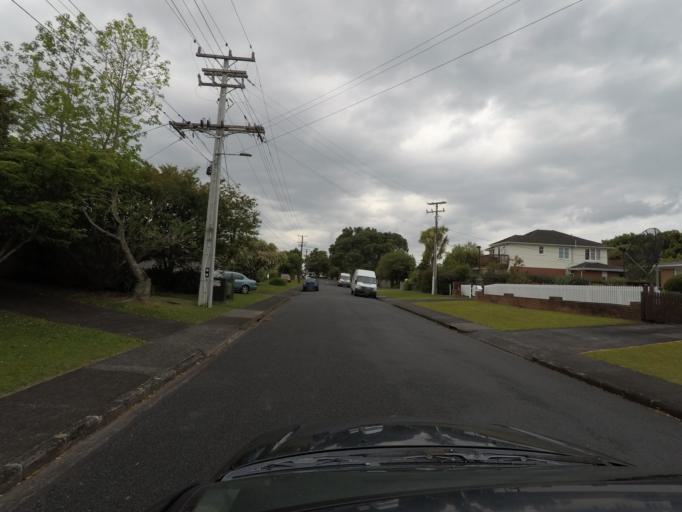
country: NZ
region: Auckland
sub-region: Auckland
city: Rosebank
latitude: -36.8468
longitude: 174.6501
